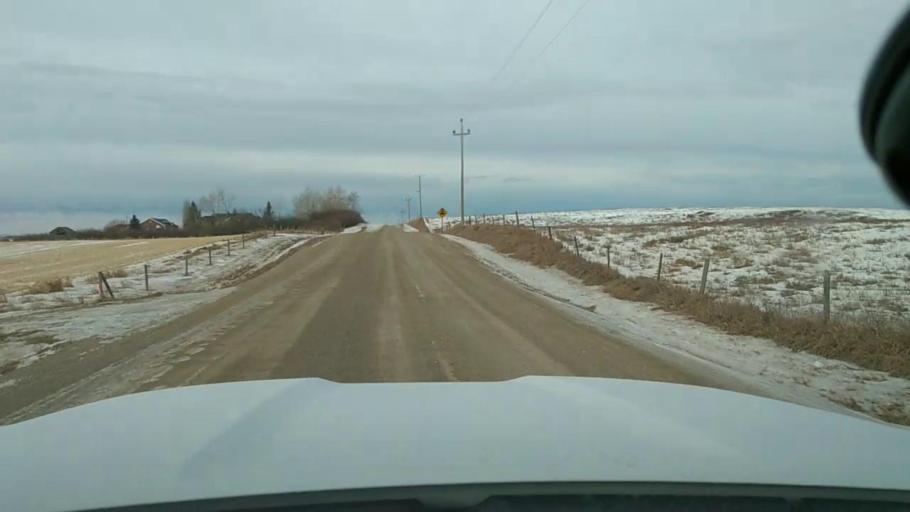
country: CA
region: Alberta
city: Airdrie
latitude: 51.2417
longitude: -113.9170
